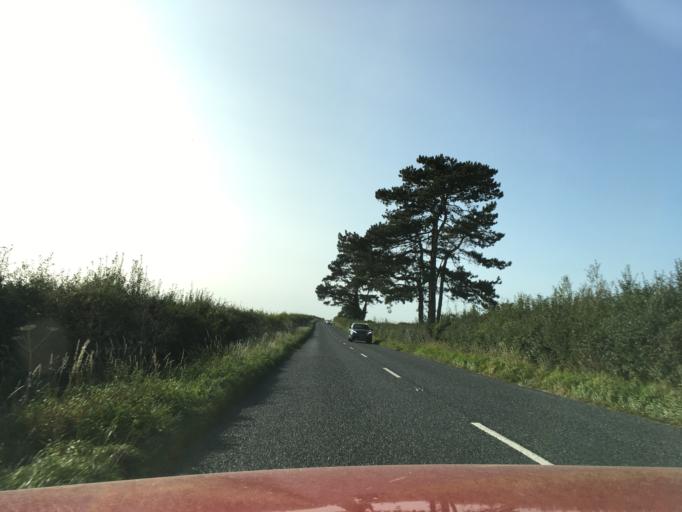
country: GB
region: England
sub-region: Gloucestershire
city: Tewkesbury
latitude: 51.9585
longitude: -2.1651
